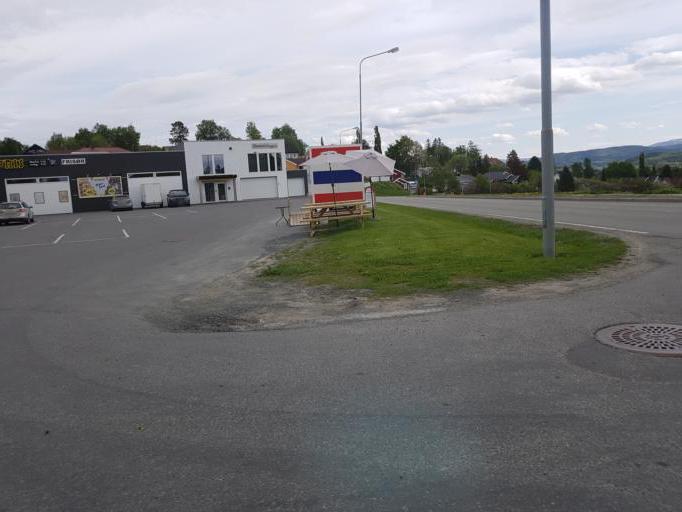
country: NO
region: Nord-Trondelag
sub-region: Levanger
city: Levanger
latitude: 63.7491
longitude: 11.2727
